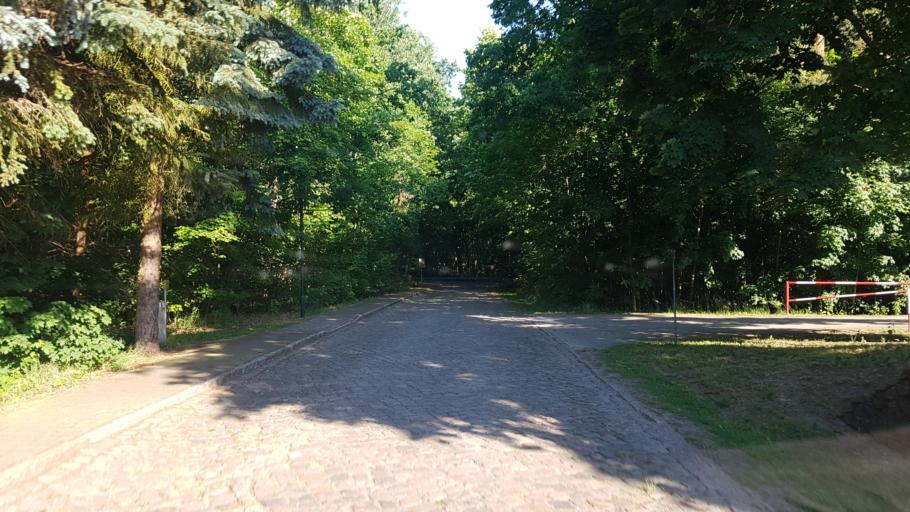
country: DE
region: Brandenburg
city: Lebusa
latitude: 51.7837
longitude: 13.3952
